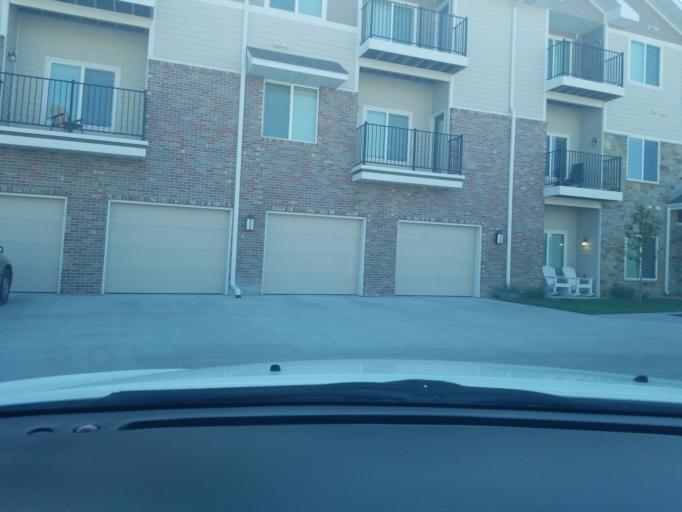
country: US
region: Nebraska
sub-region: Lancaster County
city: Lincoln
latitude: 40.7390
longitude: -96.6004
